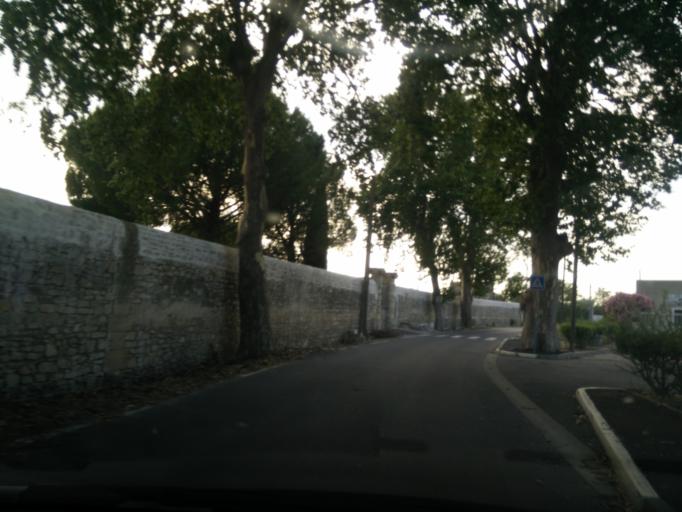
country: FR
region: Languedoc-Roussillon
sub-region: Departement de l'Herault
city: Marsillargues
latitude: 43.6716
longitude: 4.1754
